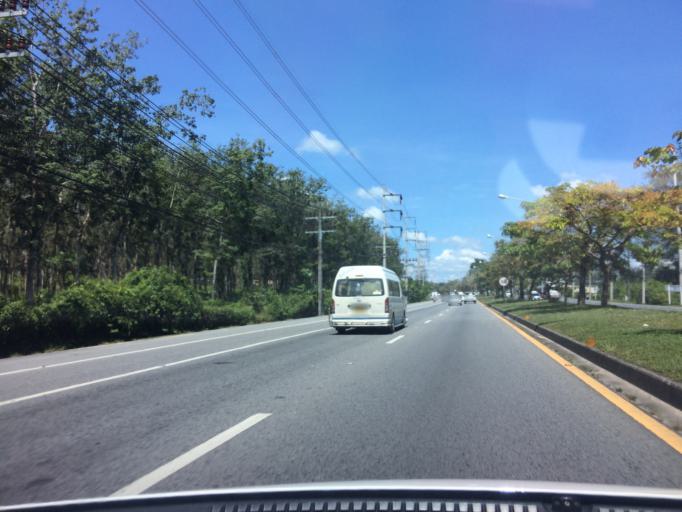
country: TH
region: Phuket
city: Thalang
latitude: 8.1152
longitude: 98.3357
